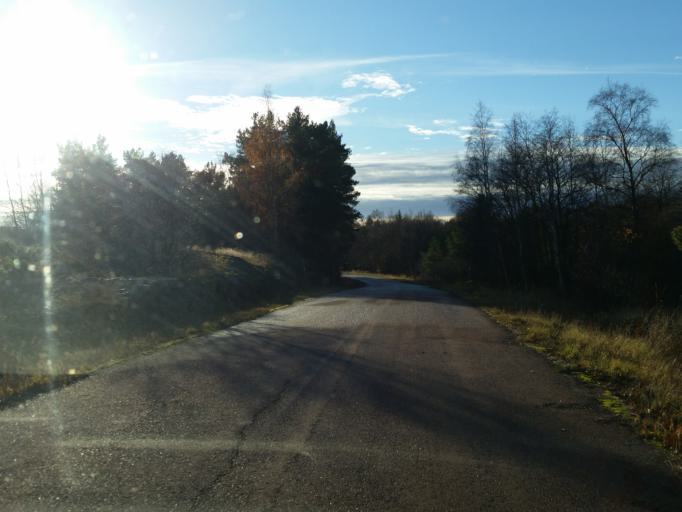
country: AX
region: Alands skaergard
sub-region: Sottunga
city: Sottunga
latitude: 60.2098
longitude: 20.7036
